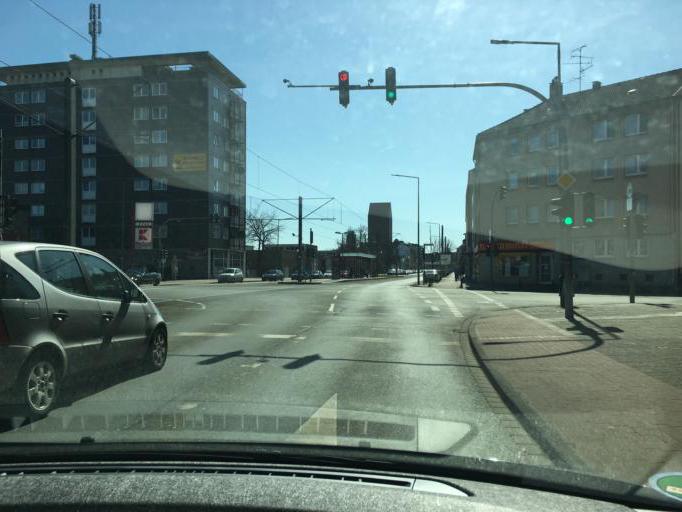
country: DE
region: North Rhine-Westphalia
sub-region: Regierungsbezirk Dusseldorf
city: Duisburg
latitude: 51.4412
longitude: 6.7516
